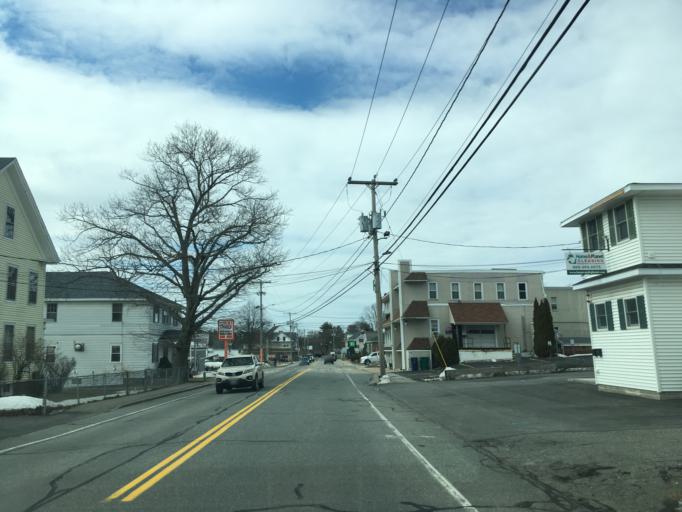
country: US
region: New Hampshire
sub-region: Rockingham County
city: Hampton
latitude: 42.9409
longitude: -70.8349
